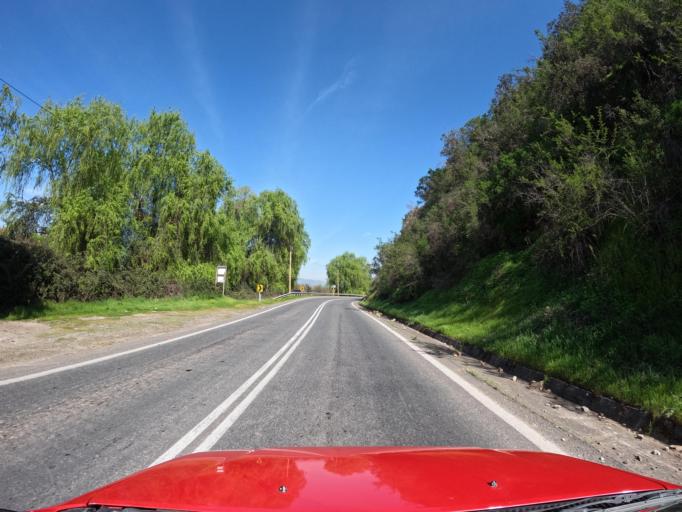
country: CL
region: Maule
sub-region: Provincia de Curico
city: Rauco
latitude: -34.9894
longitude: -71.4301
